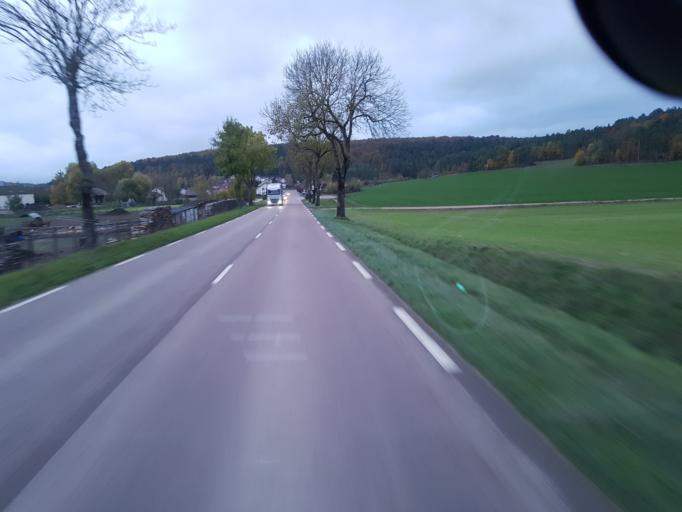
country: FR
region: Champagne-Ardenne
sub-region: Departement de l'Aube
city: Mussy-sur-Seine
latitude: 47.9913
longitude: 4.4838
